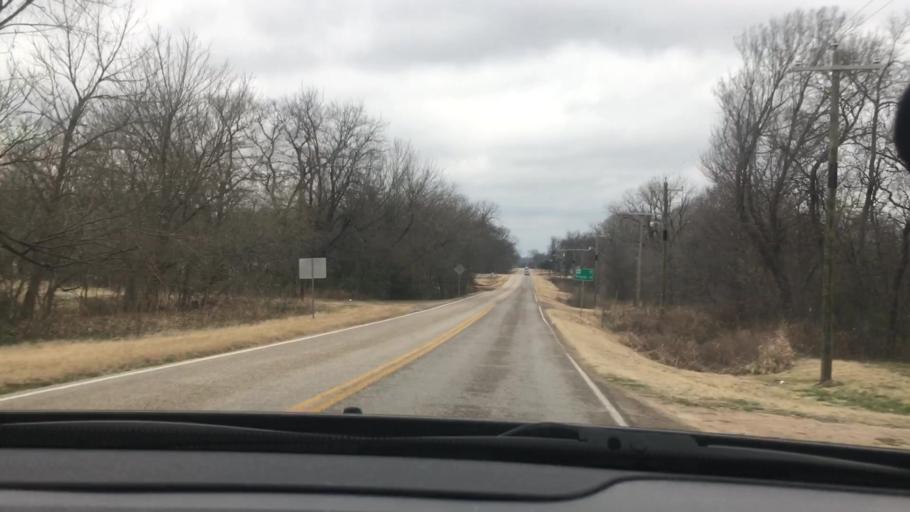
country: US
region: Oklahoma
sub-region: Coal County
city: Coalgate
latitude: 34.3750
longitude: -96.4261
